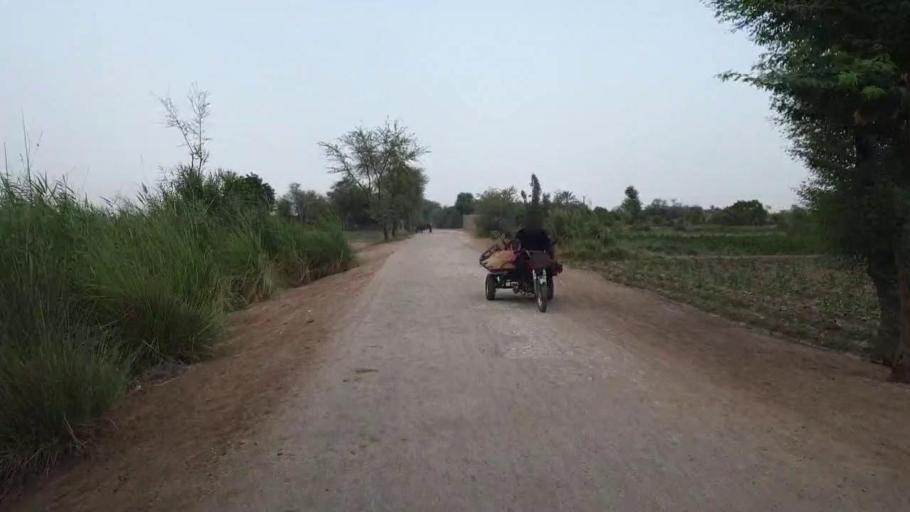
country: PK
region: Sindh
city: Bandhi
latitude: 26.5320
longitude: 68.2058
